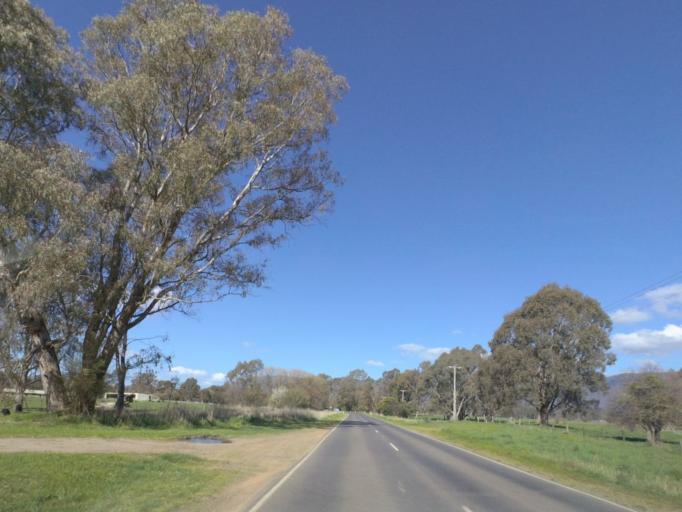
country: AU
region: Victoria
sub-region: Murrindindi
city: Alexandra
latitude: -37.2529
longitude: 145.7883
